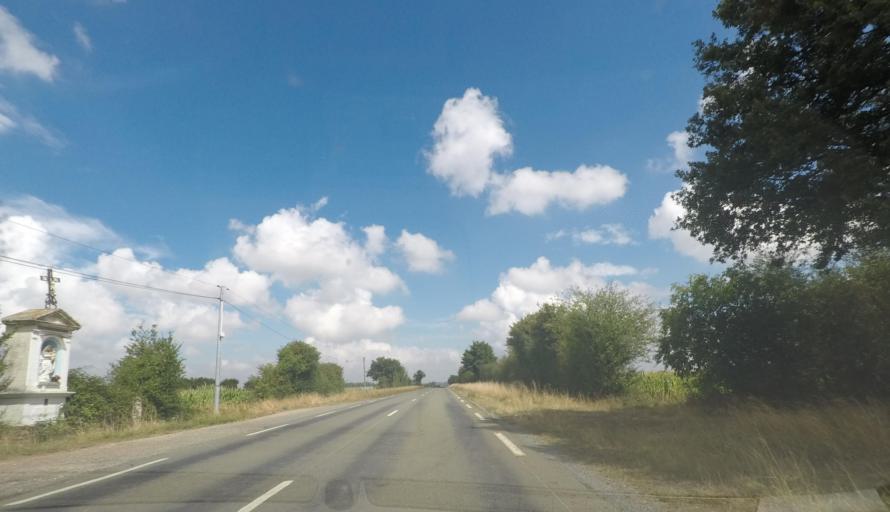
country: FR
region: Pays de la Loire
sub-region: Departement de la Sarthe
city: Saint-Cosme-en-Vairais
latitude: 48.2436
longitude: 0.4417
